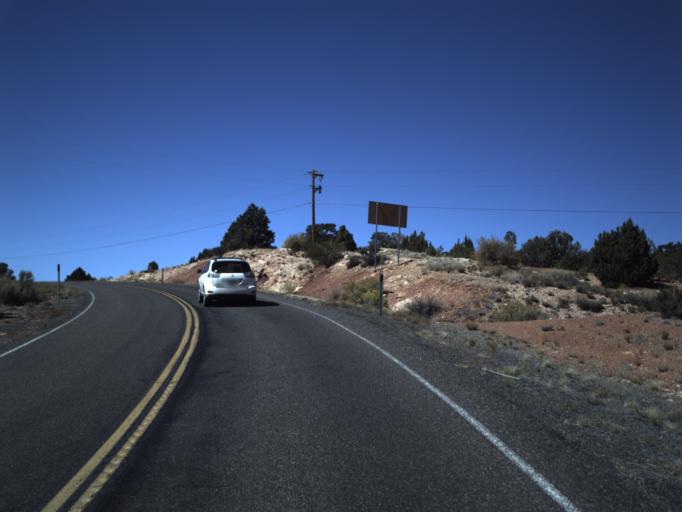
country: US
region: Utah
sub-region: Wayne County
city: Loa
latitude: 37.7503
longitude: -111.4572
